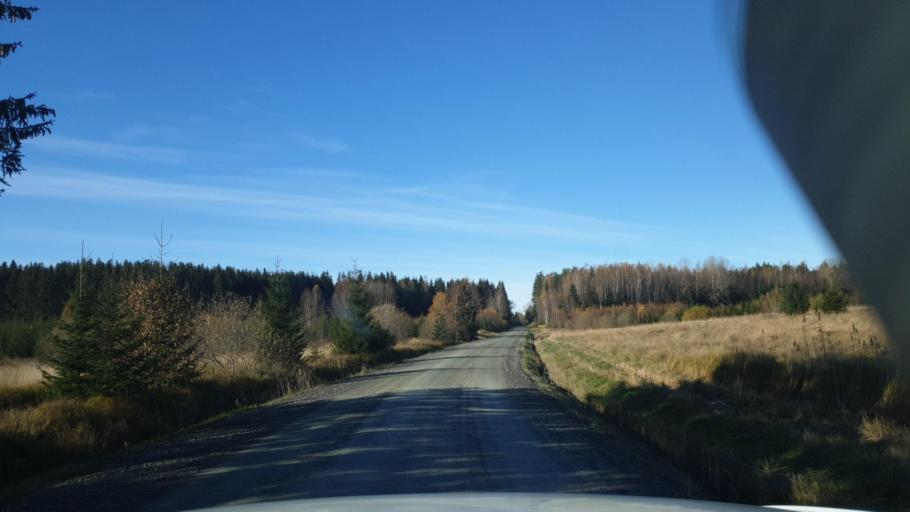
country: SE
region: Vaermland
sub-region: Karlstads Kommun
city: Edsvalla
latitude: 59.4504
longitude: 13.1383
